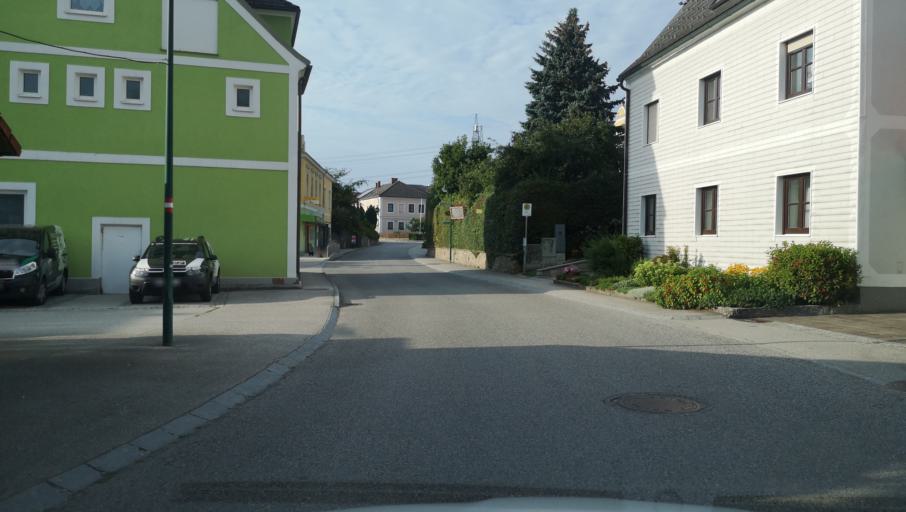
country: AT
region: Lower Austria
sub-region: Politischer Bezirk Amstetten
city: Amstetten
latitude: 48.1506
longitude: 14.8945
